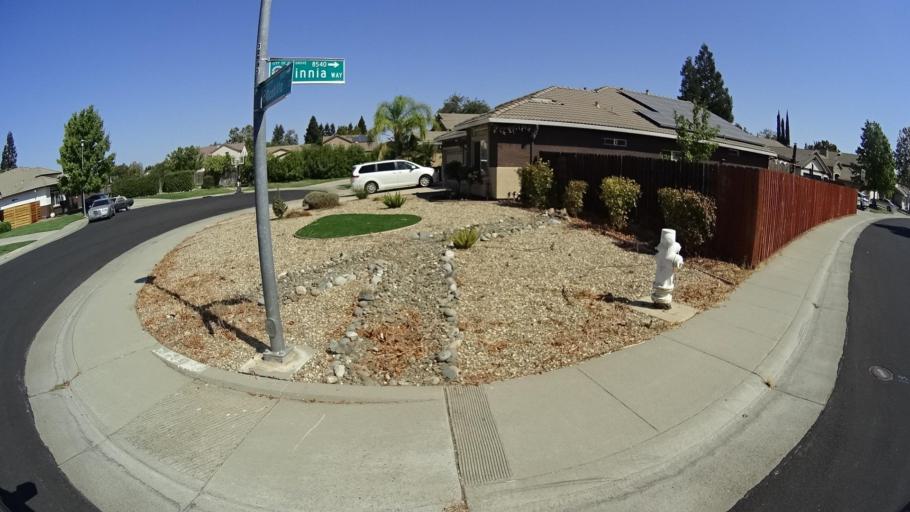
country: US
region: California
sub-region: Sacramento County
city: Elk Grove
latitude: 38.4482
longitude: -121.3884
